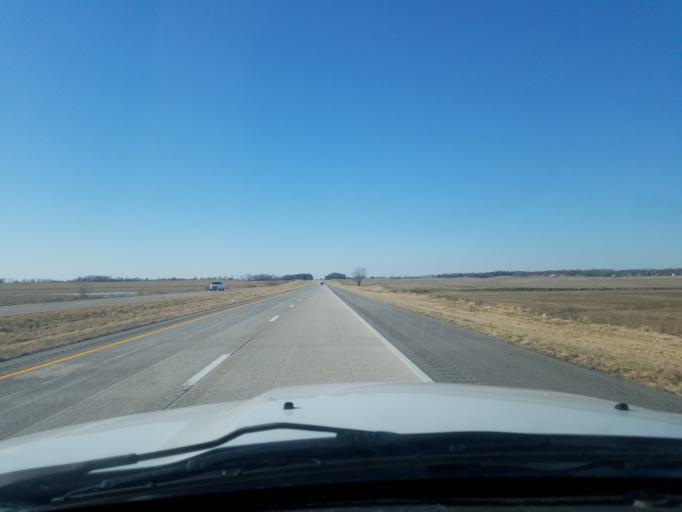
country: US
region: Kentucky
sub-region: Henderson County
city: Henderson
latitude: 37.8005
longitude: -87.5147
